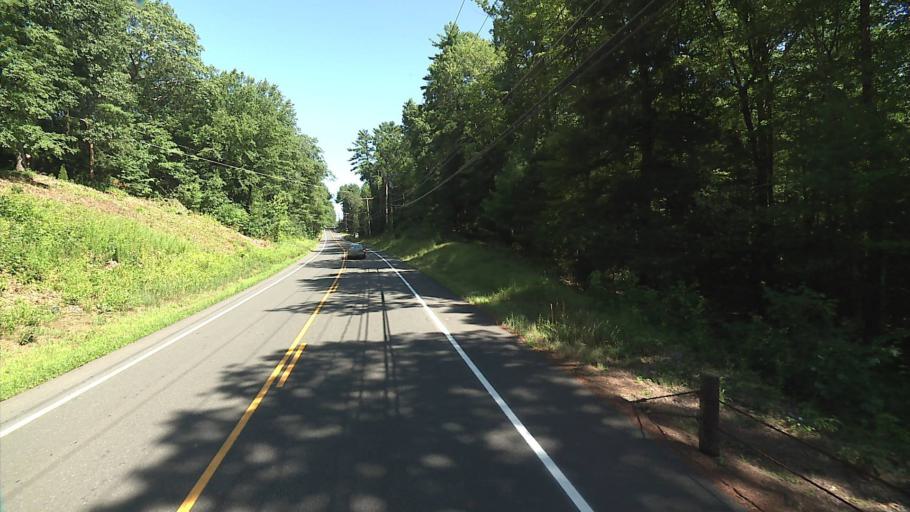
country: US
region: Connecticut
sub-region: Hartford County
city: Salmon Brook
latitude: 41.9776
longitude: -72.7988
